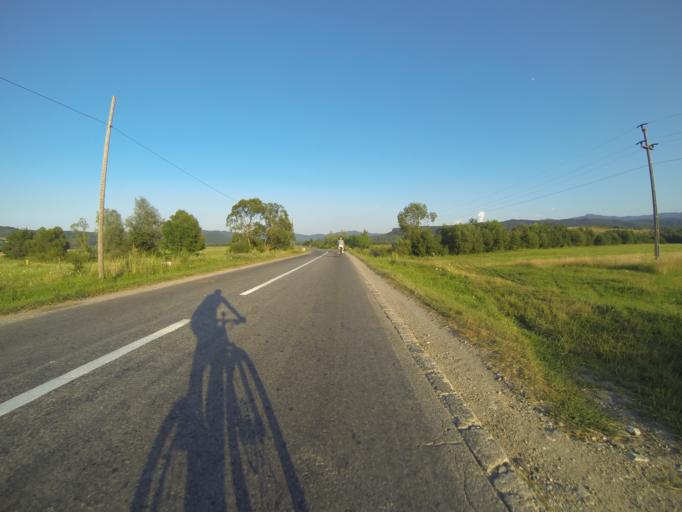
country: RO
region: Brasov
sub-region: Comuna Sinca Veche
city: Sinca Veche
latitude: 45.7506
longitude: 25.1826
